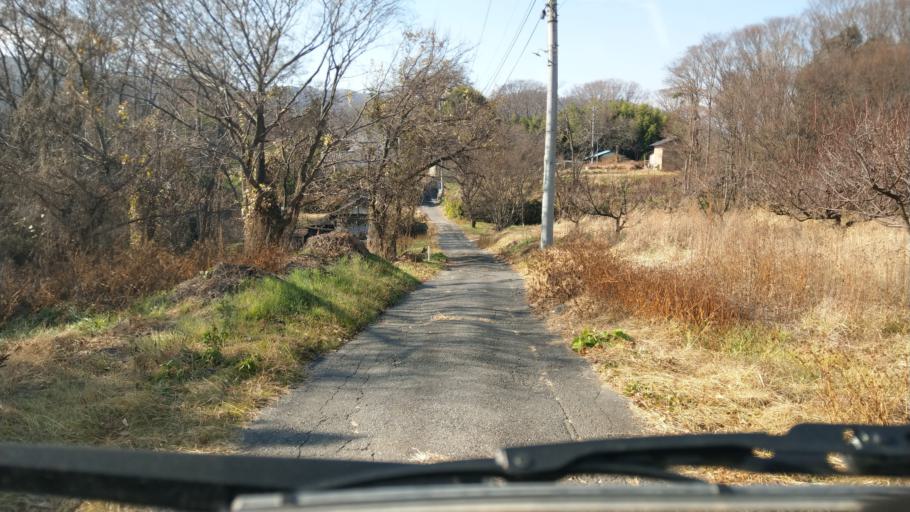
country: JP
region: Nagano
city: Komoro
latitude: 36.3189
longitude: 138.4245
